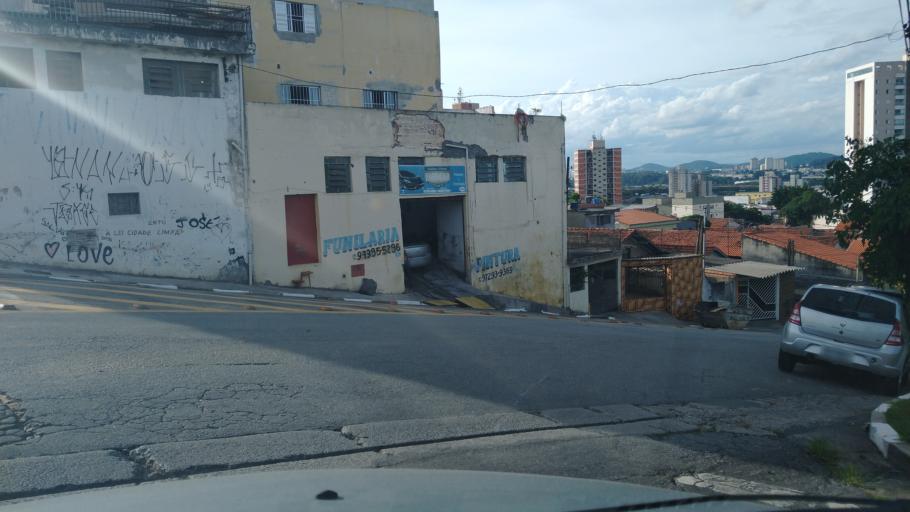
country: BR
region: Sao Paulo
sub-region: Osasco
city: Osasco
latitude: -23.5312
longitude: -46.8106
